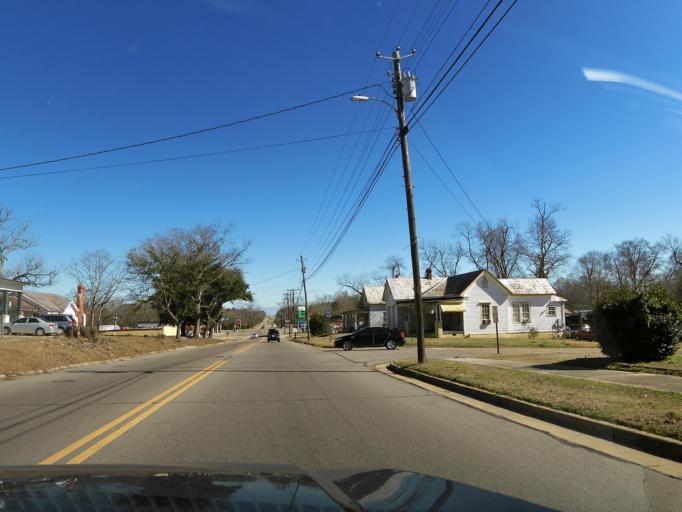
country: US
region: Alabama
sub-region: Bullock County
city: Union Springs
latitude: 32.1462
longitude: -85.7110
